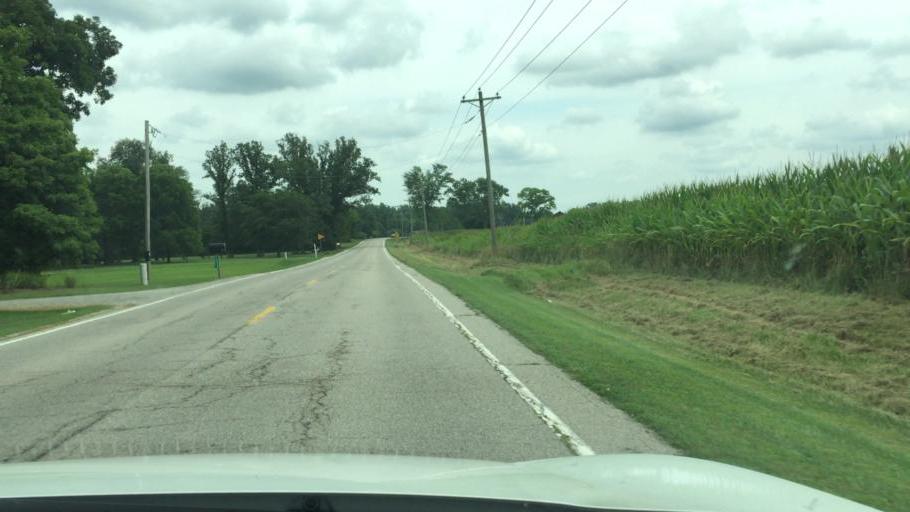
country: US
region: Ohio
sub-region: Champaign County
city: North Lewisburg
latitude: 40.2352
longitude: -83.4677
